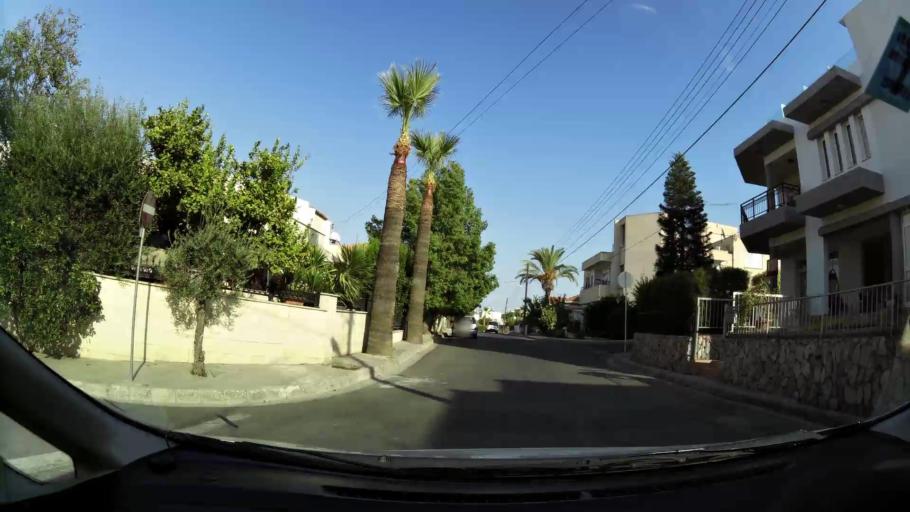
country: CY
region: Lefkosia
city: Nicosia
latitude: 35.1732
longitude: 33.3322
